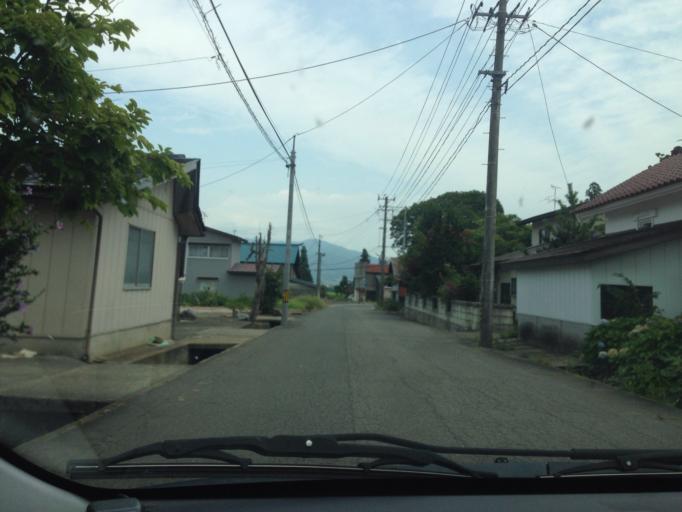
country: JP
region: Fukushima
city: Kitakata
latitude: 37.6344
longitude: 139.8360
